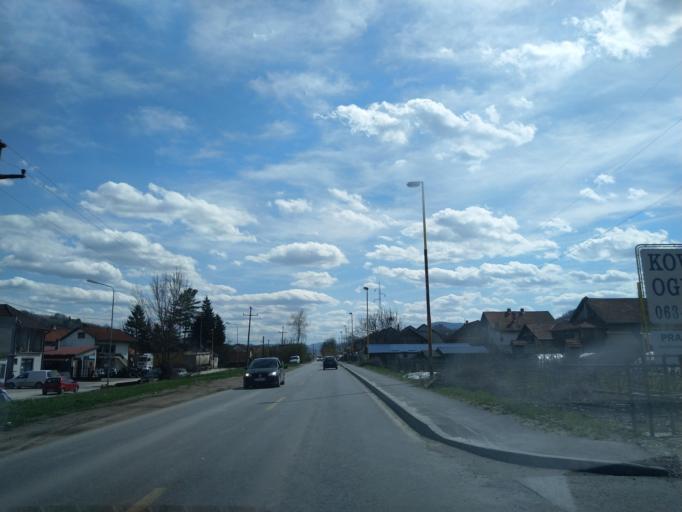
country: RS
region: Central Serbia
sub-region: Zlatiborski Okrug
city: Arilje
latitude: 43.7508
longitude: 20.1049
